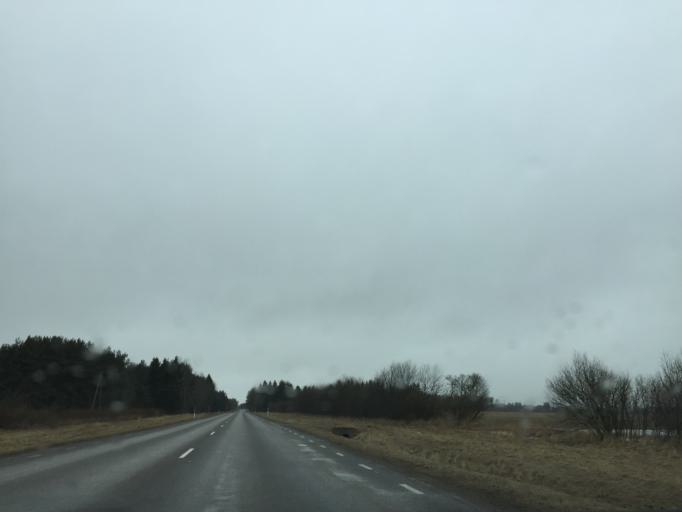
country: EE
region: Laeaene
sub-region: Ridala Parish
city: Uuemoisa
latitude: 58.8708
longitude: 23.6178
